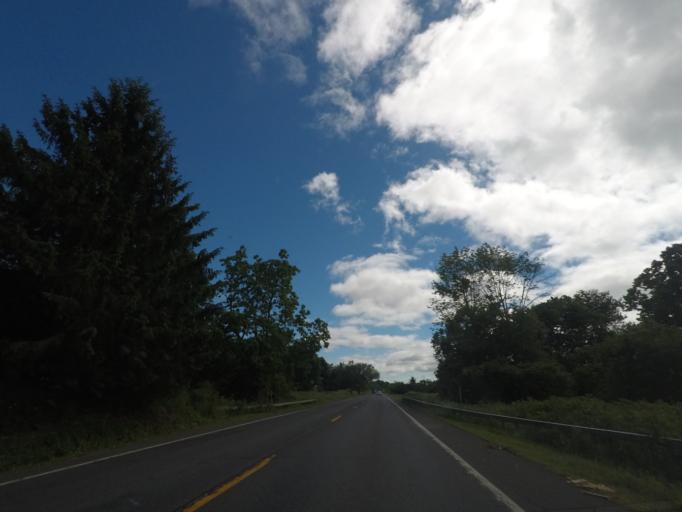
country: US
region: New York
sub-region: Columbia County
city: Philmont
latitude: 42.1435
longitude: -73.5232
